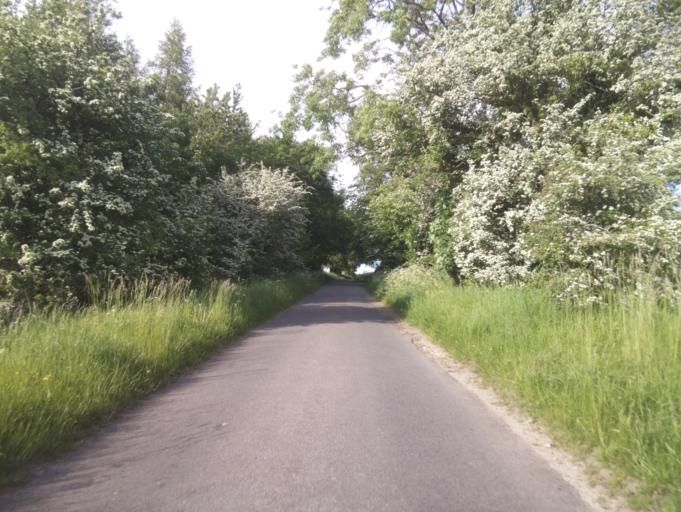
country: GB
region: England
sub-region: Gloucestershire
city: Stow on the Wold
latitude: 51.9423
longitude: -1.7920
